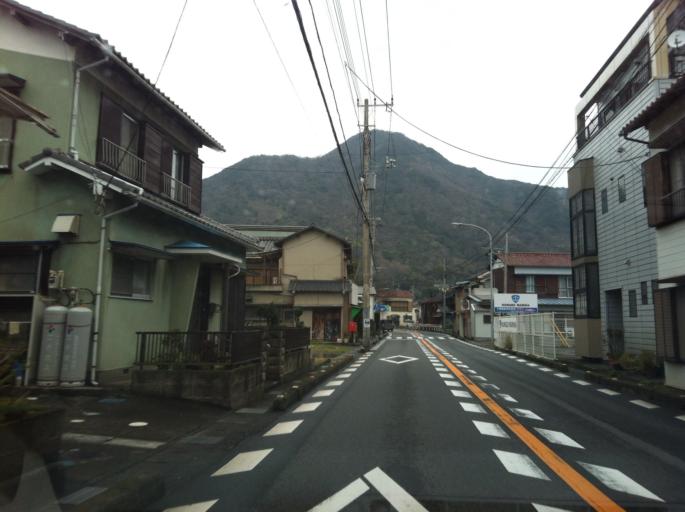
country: JP
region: Shizuoka
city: Numazu
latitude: 35.0479
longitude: 138.8905
